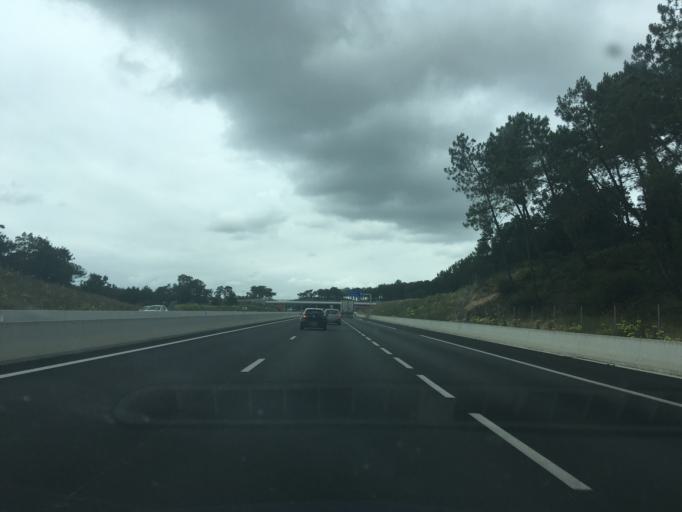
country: FR
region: Aquitaine
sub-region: Departement des Landes
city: Labenne
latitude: 43.5918
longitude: -1.4177
